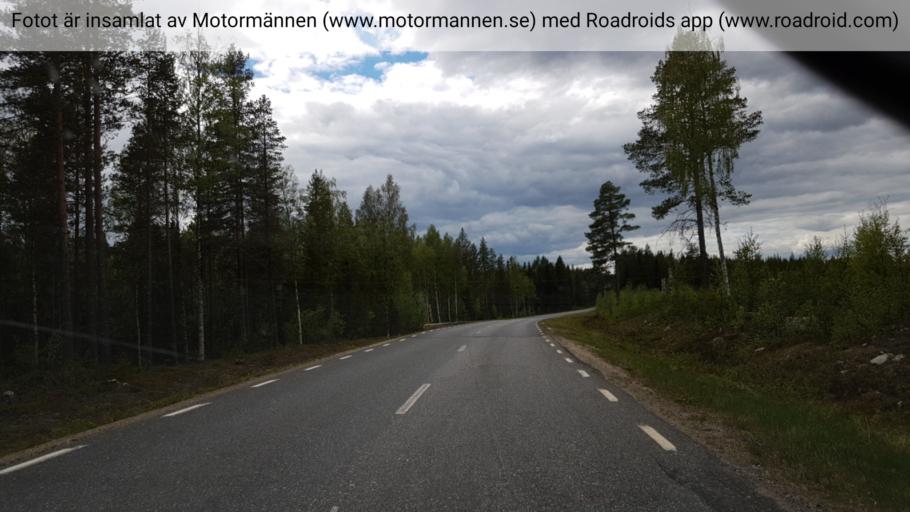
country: SE
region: Vaesterbotten
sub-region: Vindelns Kommun
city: Vindeln
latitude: 64.5267
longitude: 19.8558
